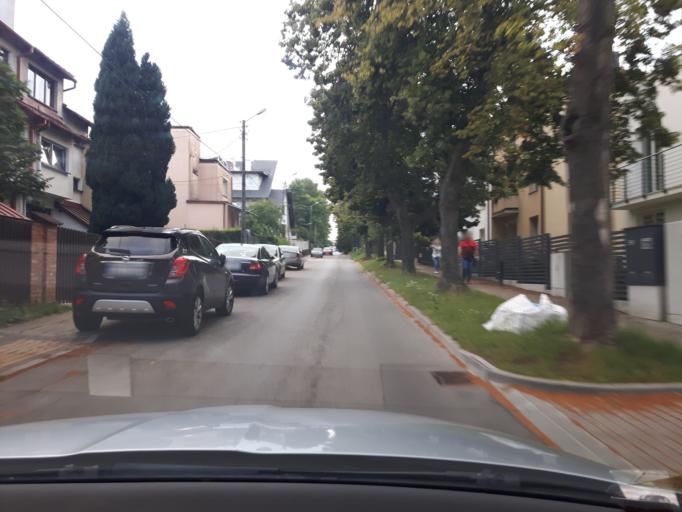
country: PL
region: Pomeranian Voivodeship
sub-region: Sopot
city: Sopot
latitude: 54.4789
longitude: 18.5563
